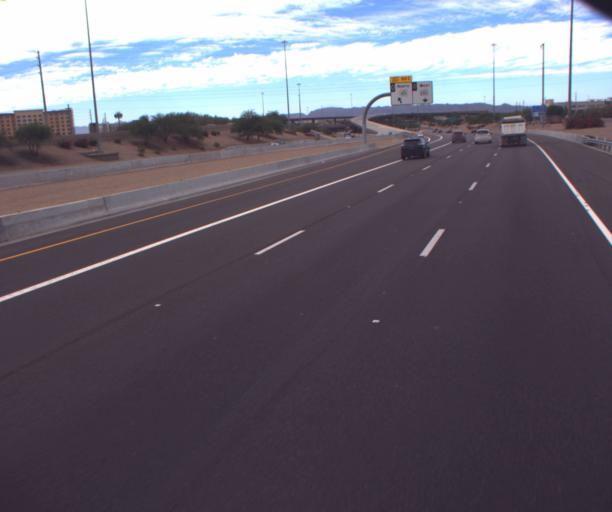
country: US
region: Arizona
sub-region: Maricopa County
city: Chandler
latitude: 33.2902
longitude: -111.8849
